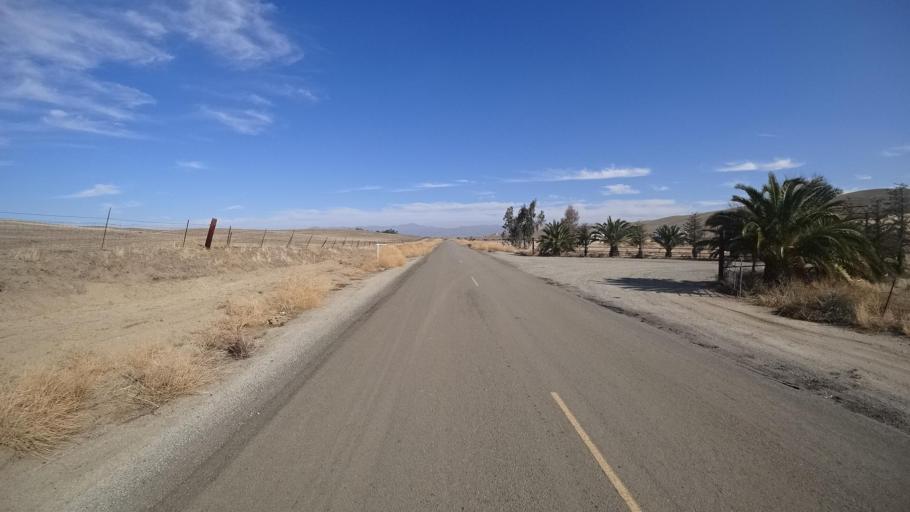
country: US
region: California
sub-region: Kern County
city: Oildale
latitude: 35.6275
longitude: -118.9785
